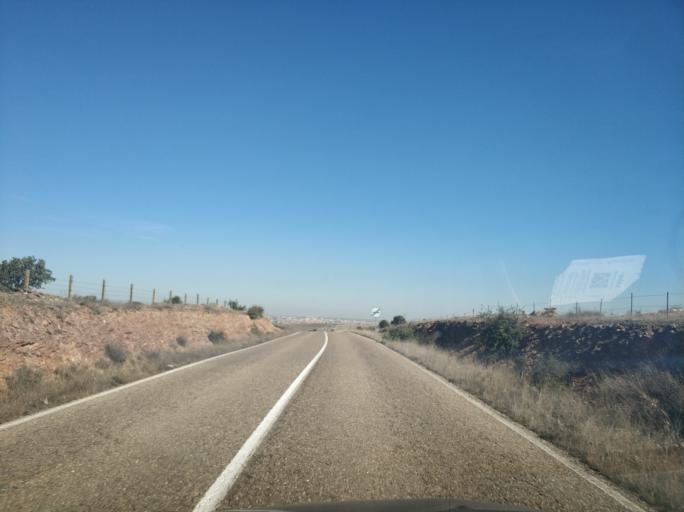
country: ES
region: Castille and Leon
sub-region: Provincia de Salamanca
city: Doninos de Salamanca
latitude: 40.9326
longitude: -5.7255
